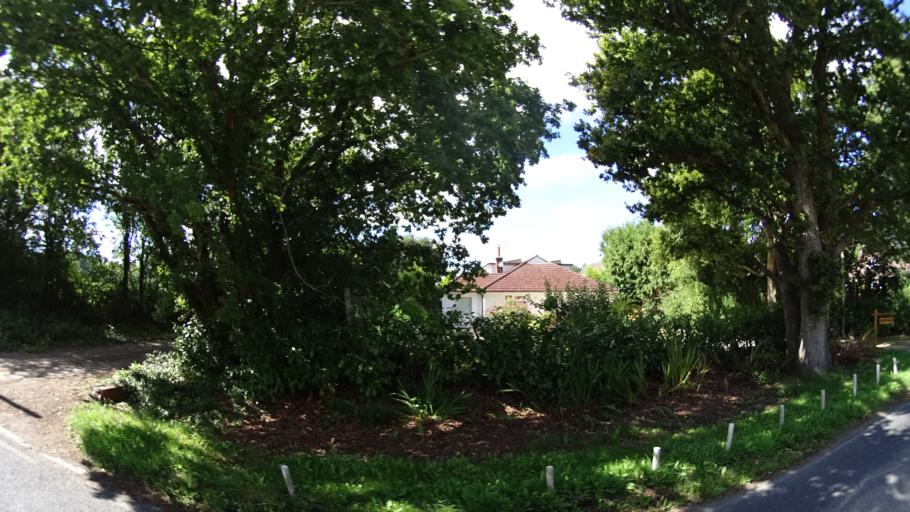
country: GB
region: England
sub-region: Hampshire
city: Romsey
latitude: 51.0106
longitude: -1.4718
